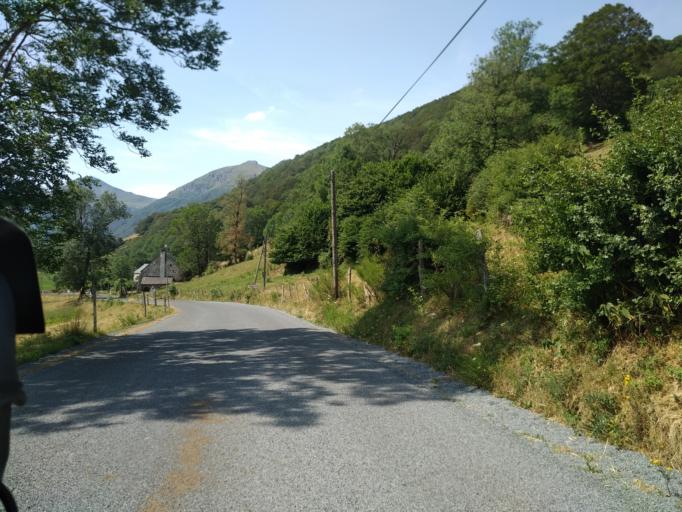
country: FR
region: Auvergne
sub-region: Departement du Cantal
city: Riom-es-Montagnes
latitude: 45.1493
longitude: 2.6992
